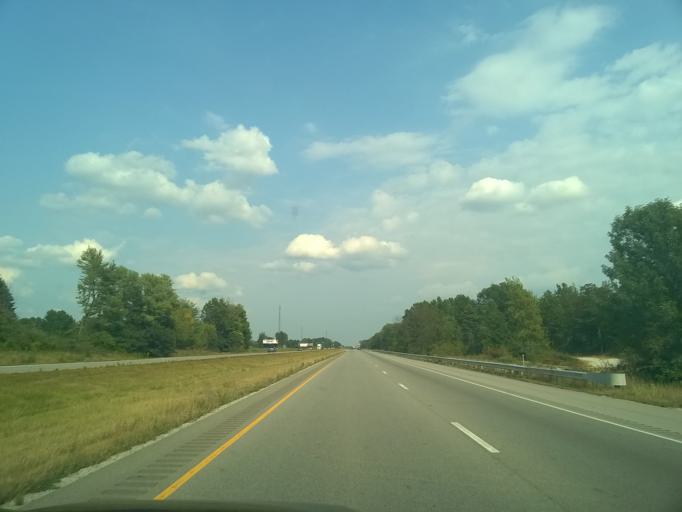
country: US
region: Indiana
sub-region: Vigo County
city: Seelyville
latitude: 39.4457
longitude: -87.2467
